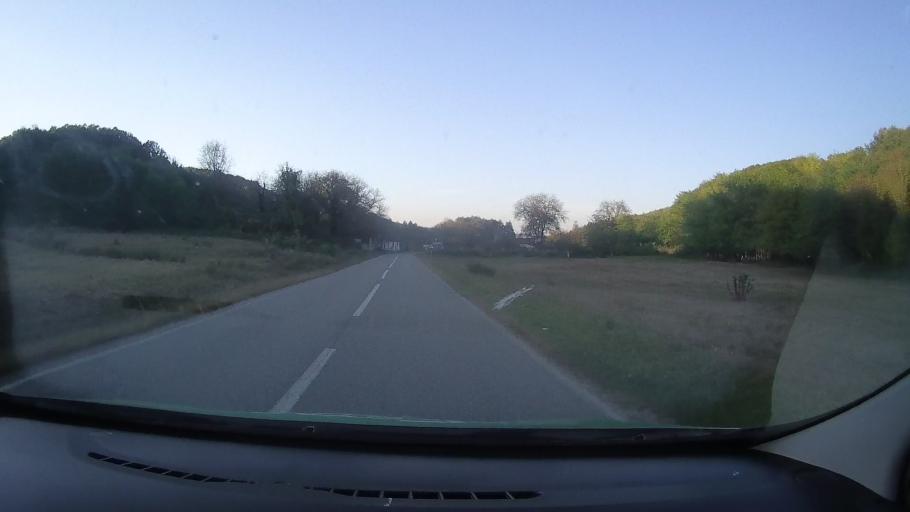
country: RO
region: Timis
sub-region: Comuna Fardea
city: Fardea
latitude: 45.7073
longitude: 22.1605
